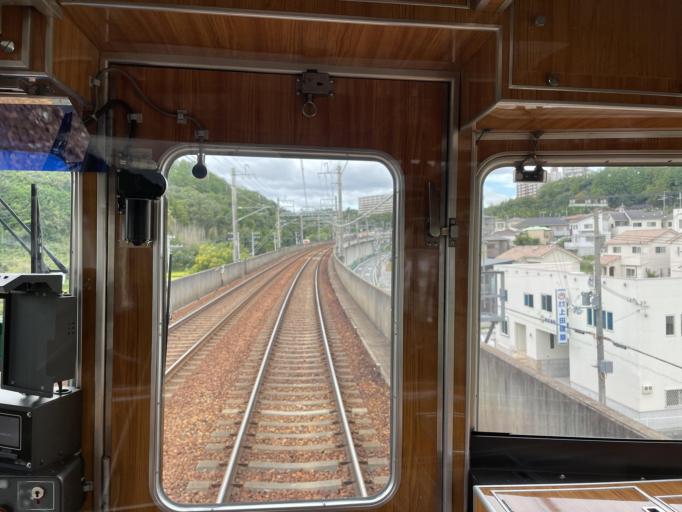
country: JP
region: Osaka
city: Ikeda
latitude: 34.9013
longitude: 135.4025
